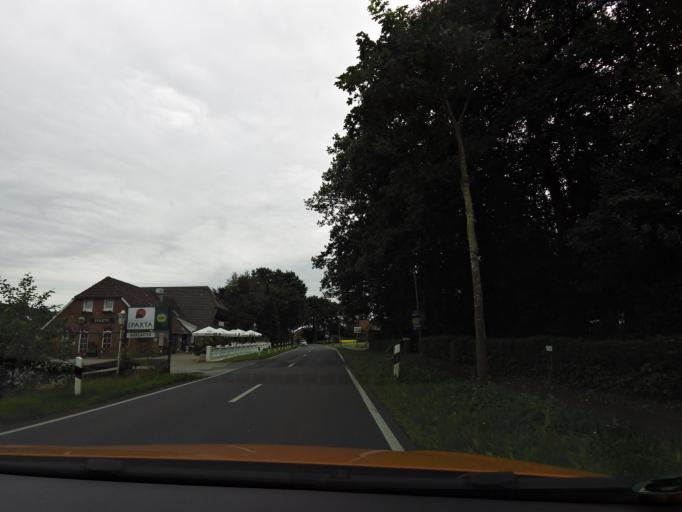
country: DE
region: Lower Saxony
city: Wiefelstede
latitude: 53.1894
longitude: 8.1527
